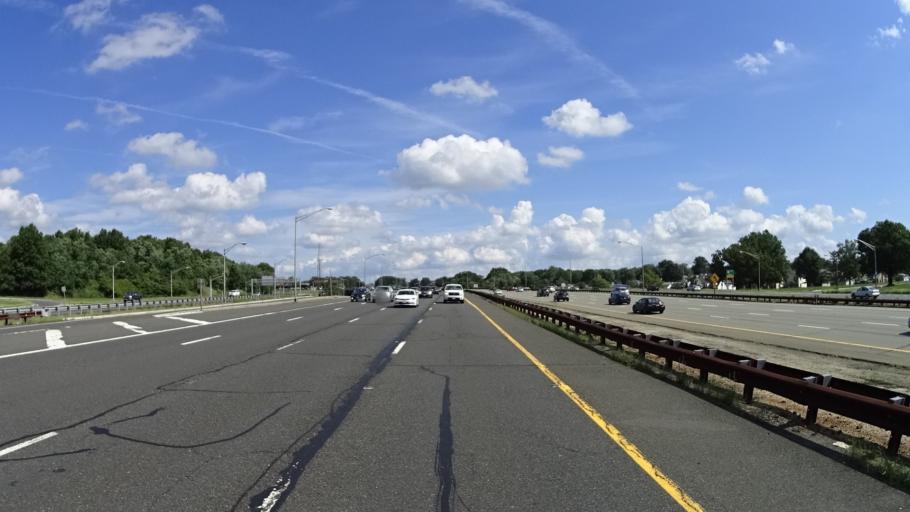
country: US
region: New Jersey
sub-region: Middlesex County
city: Fords
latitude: 40.5258
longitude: -74.2990
